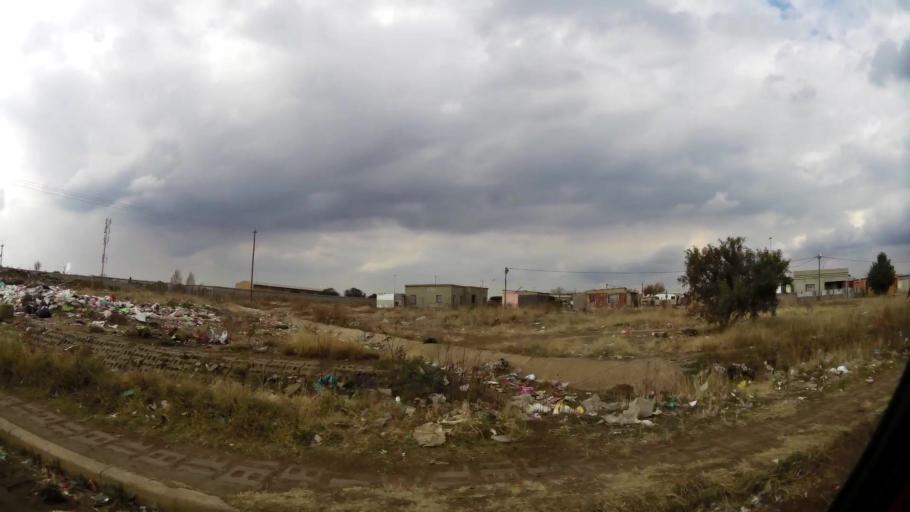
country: ZA
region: Gauteng
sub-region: Sedibeng District Municipality
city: Vanderbijlpark
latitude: -26.6967
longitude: 27.7842
